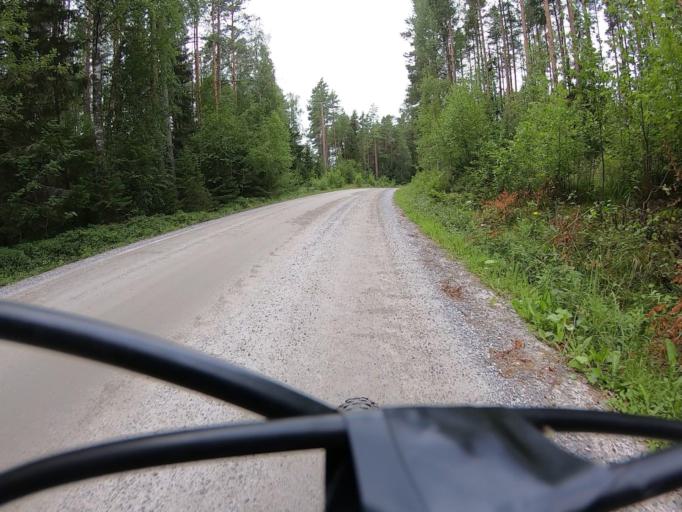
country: FI
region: Varsinais-Suomi
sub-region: Vakka-Suomi
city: Uusikaupunki
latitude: 60.8458
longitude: 21.3805
